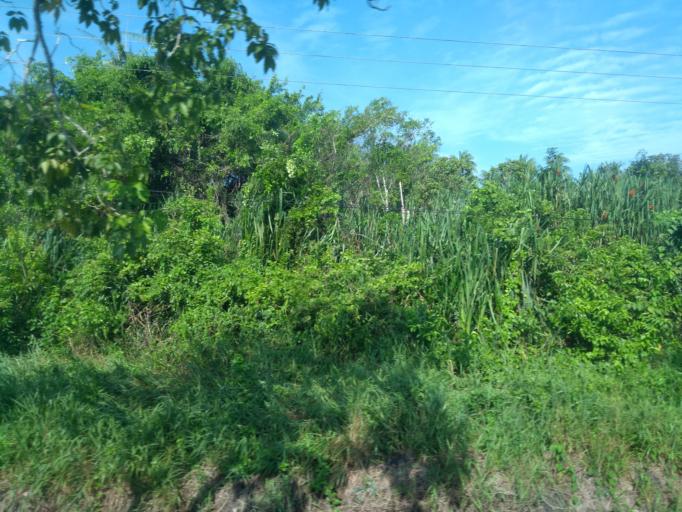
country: MY
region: Sarawak
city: Kuching
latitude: 1.6527
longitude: 110.4447
